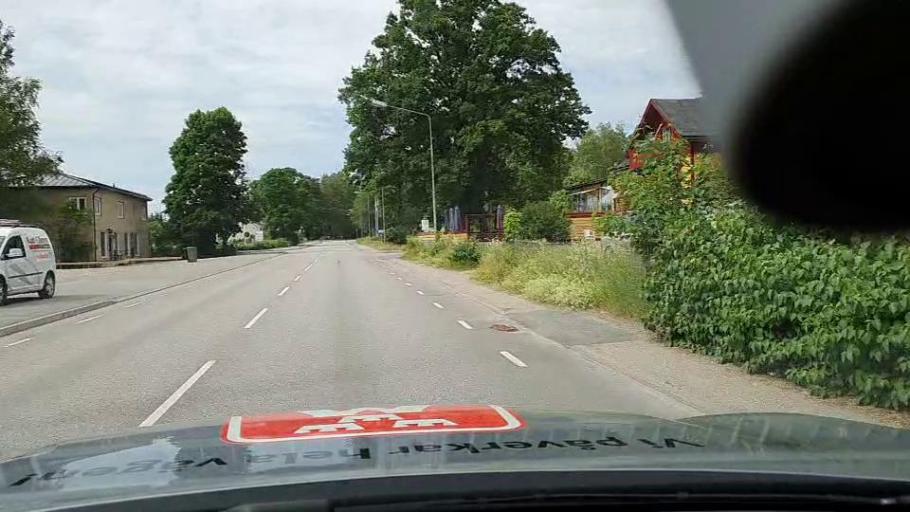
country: SE
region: Soedermanland
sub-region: Eskilstuna Kommun
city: Arla
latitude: 59.2818
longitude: 16.6779
